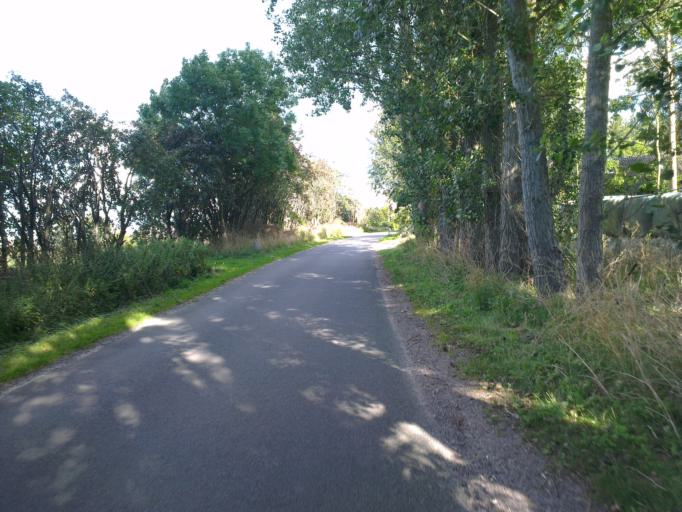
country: DK
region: Capital Region
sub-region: Frederikssund Kommune
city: Frederikssund
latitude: 55.7866
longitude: 12.0355
